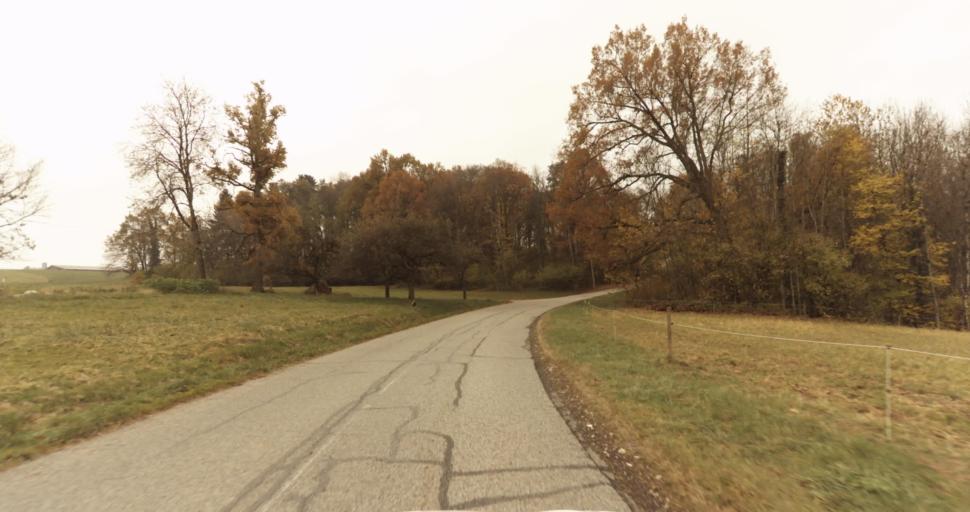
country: FR
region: Rhone-Alpes
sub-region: Departement de la Haute-Savoie
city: Saint-Felix
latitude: 45.8029
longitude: 5.9956
